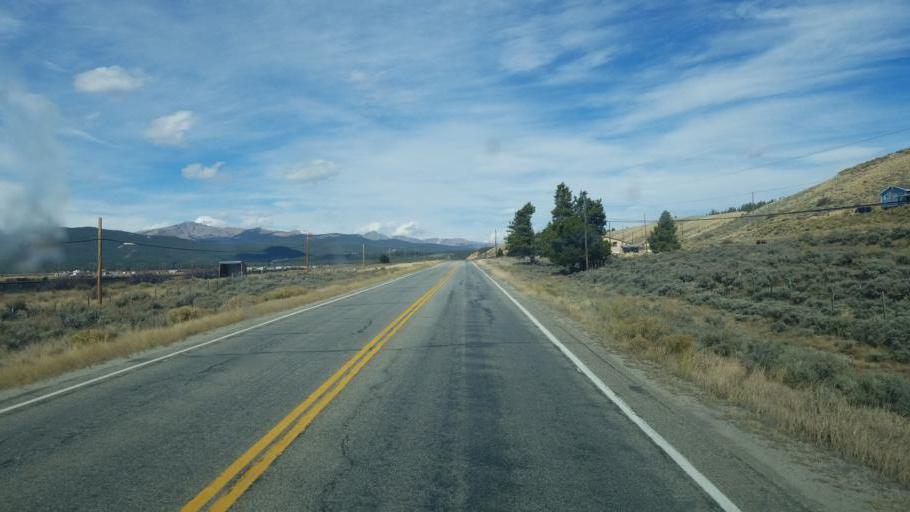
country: US
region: Colorado
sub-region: Lake County
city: Leadville North
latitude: 39.2098
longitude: -106.3457
